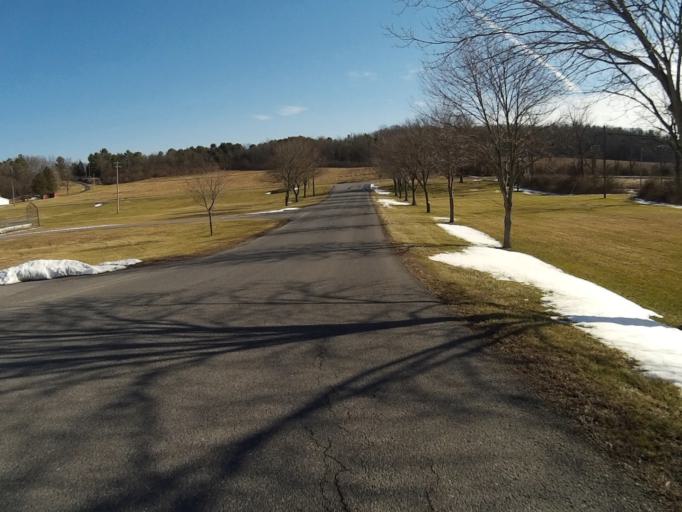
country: US
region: Pennsylvania
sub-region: Centre County
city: Houserville
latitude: 40.8664
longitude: -77.8661
